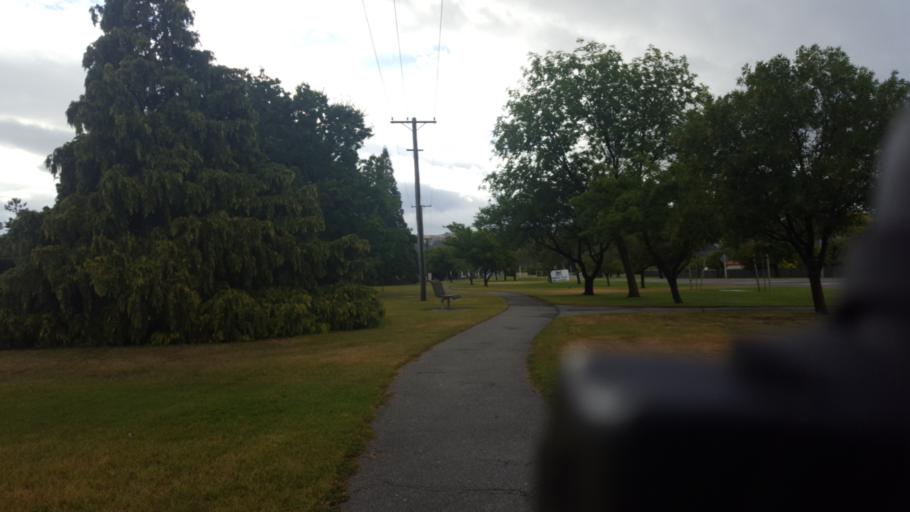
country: NZ
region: Otago
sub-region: Queenstown-Lakes District
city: Wanaka
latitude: -45.2446
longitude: 169.3802
